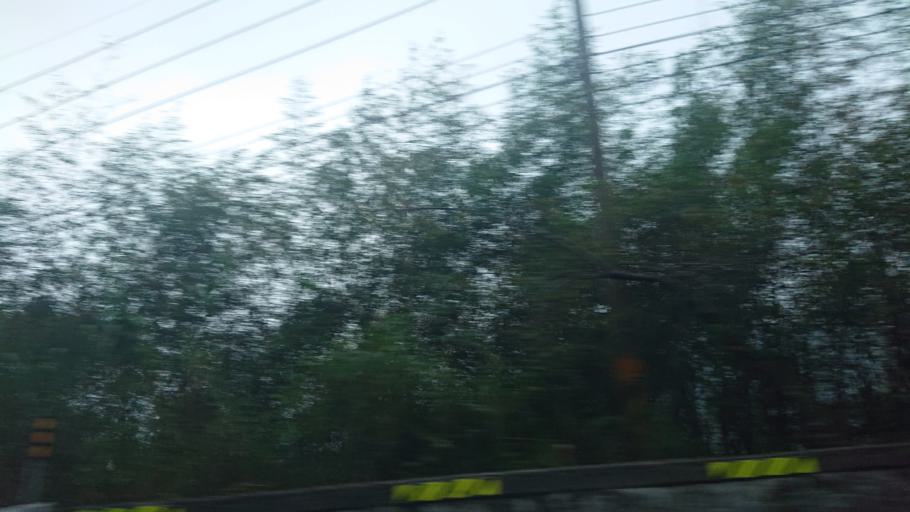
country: TW
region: Taiwan
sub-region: Chiayi
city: Jiayi Shi
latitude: 23.4732
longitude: 120.7185
